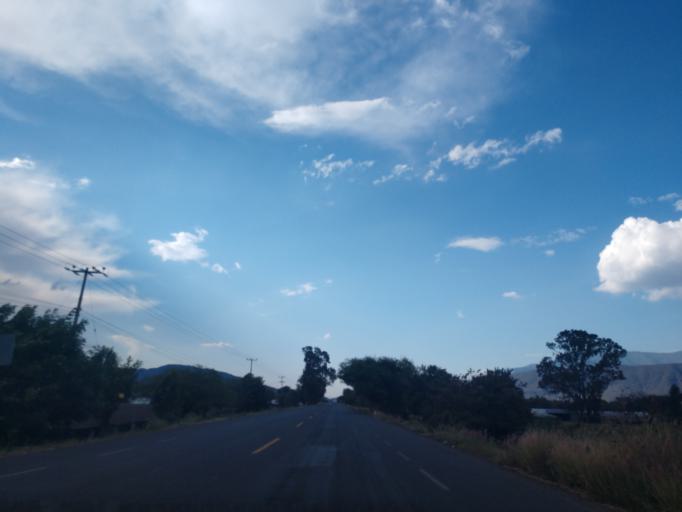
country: MX
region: Jalisco
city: Jocotepec
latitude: 20.2386
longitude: -103.4248
